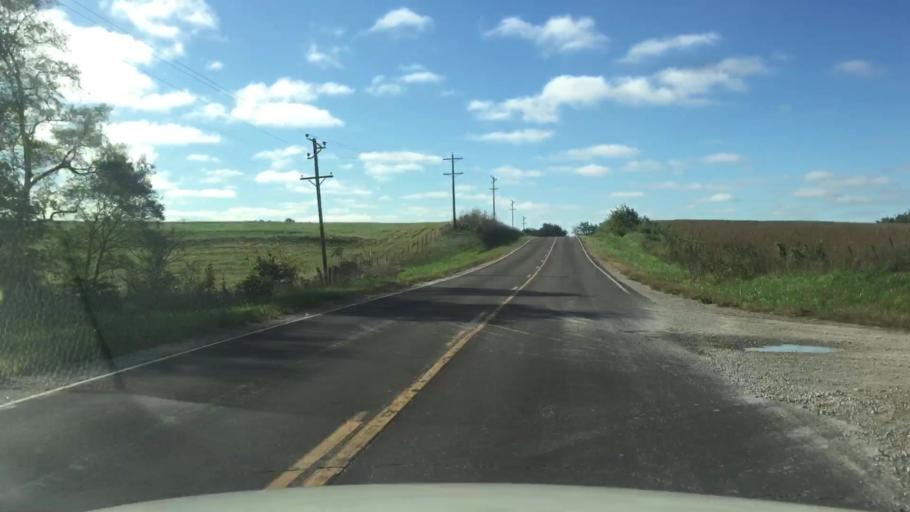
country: US
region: Missouri
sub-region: Howard County
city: New Franklin
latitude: 39.0680
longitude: -92.7461
